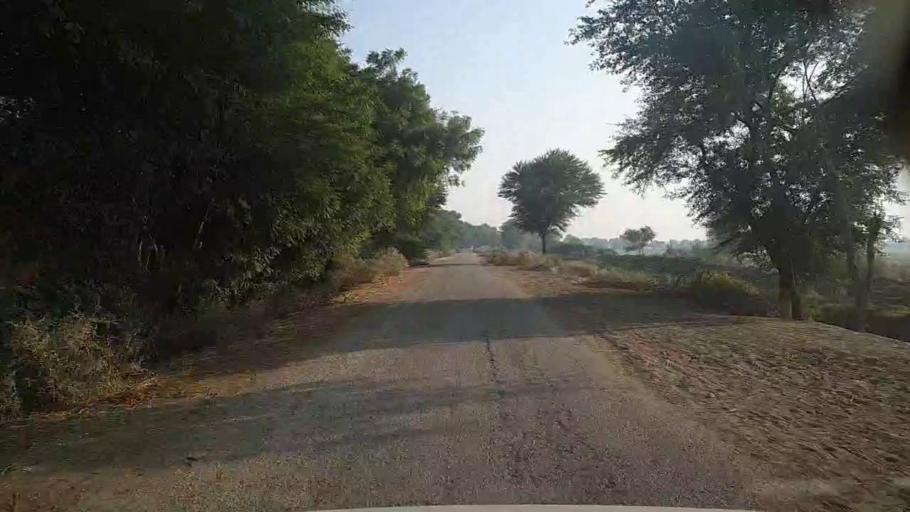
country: PK
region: Sindh
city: Karaundi
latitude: 26.7600
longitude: 68.4760
